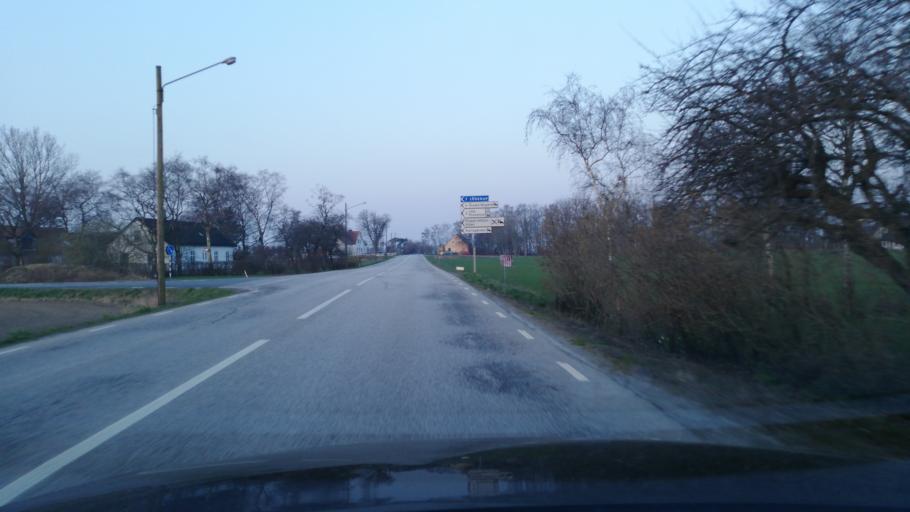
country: SE
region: Skane
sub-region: Tomelilla Kommun
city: Tomelilla
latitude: 55.4914
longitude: 14.1019
